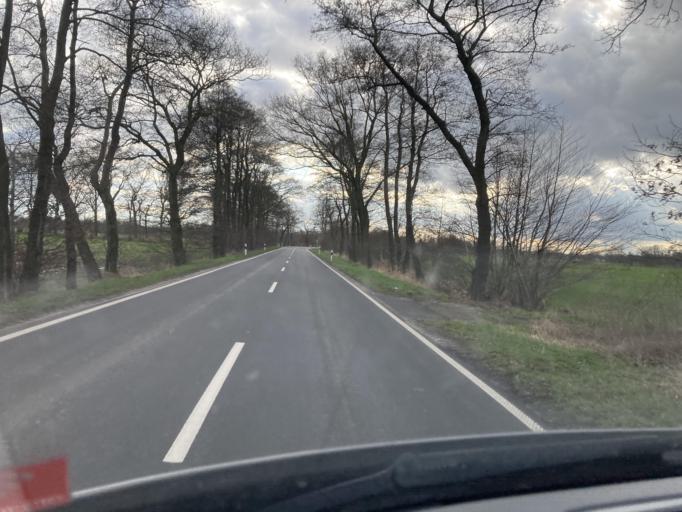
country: DE
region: Lower Saxony
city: Ostrhauderfehn
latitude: 53.1718
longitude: 7.5879
